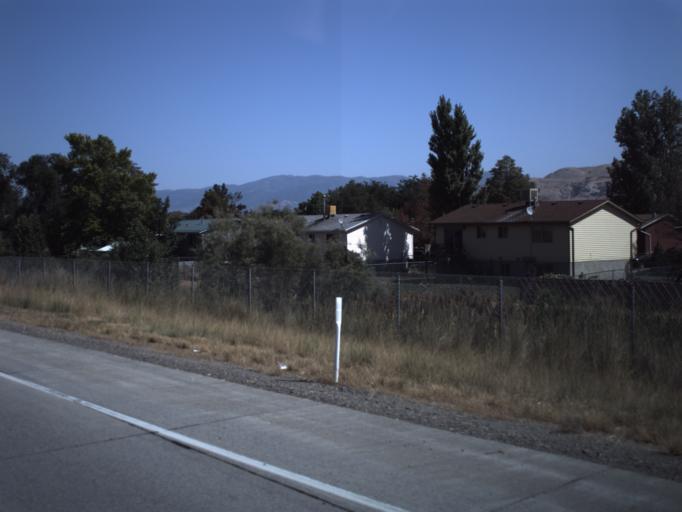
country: US
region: Utah
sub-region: Salt Lake County
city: Salt Lake City
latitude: 40.7864
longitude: -111.9485
